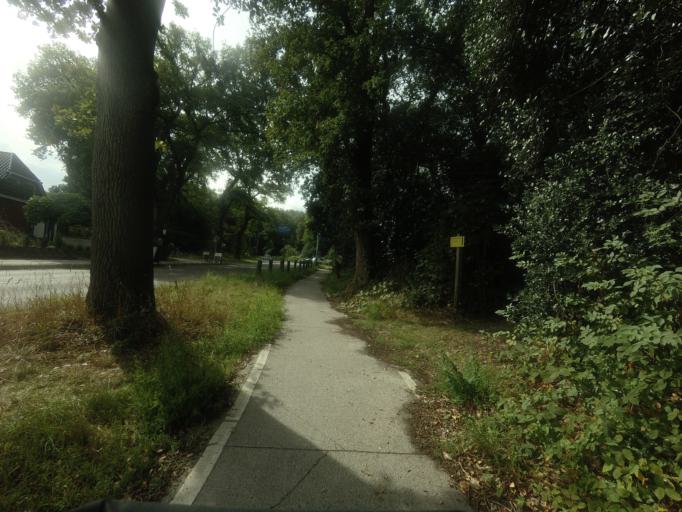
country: NL
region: Drenthe
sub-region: Gemeente Tynaarlo
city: Vries
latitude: 53.0588
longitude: 6.4552
